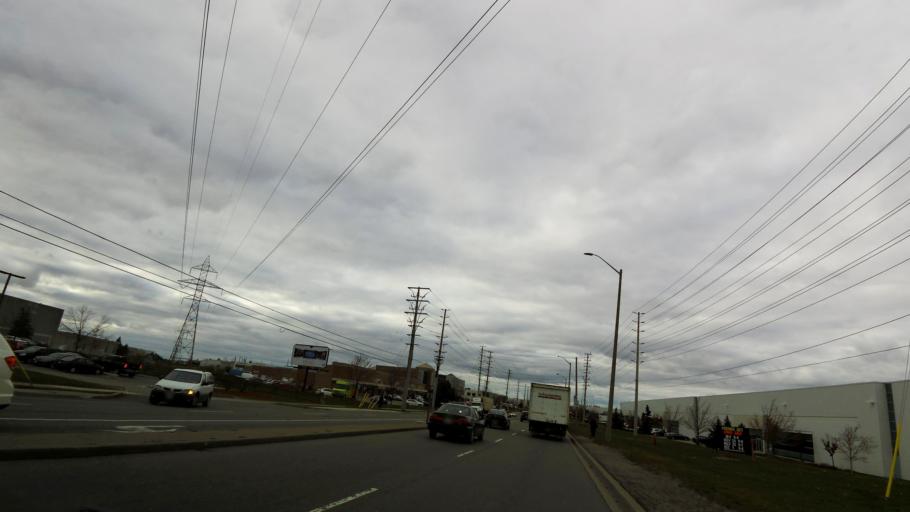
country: CA
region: Ontario
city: Mississauga
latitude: 43.6480
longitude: -79.6847
